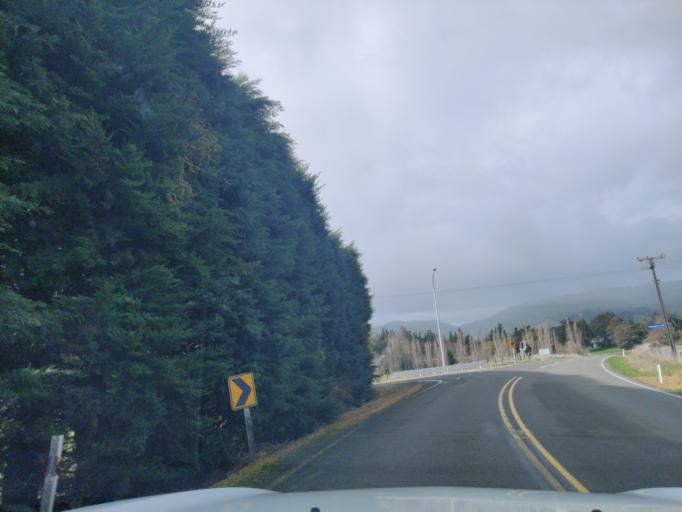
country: NZ
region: Manawatu-Wanganui
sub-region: Palmerston North City
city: Palmerston North
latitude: -40.2951
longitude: 175.7422
